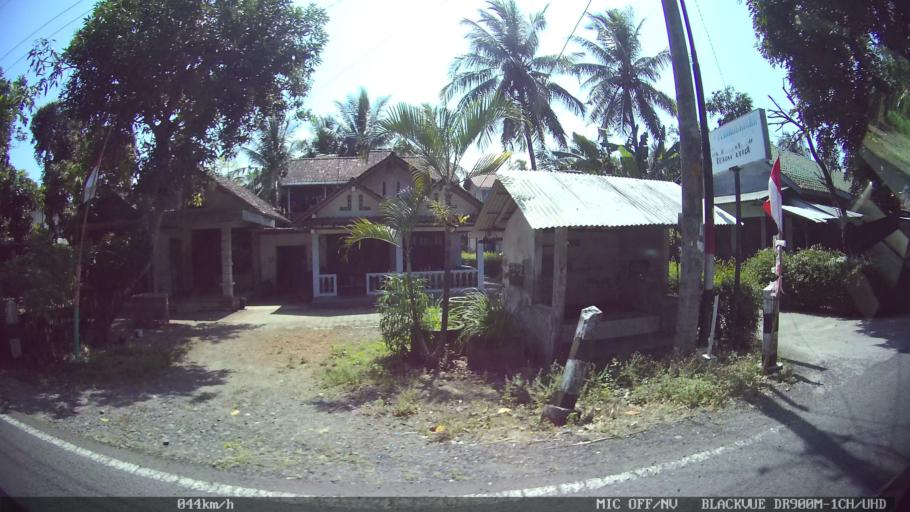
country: ID
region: Daerah Istimewa Yogyakarta
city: Srandakan
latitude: -7.8920
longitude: 110.0528
